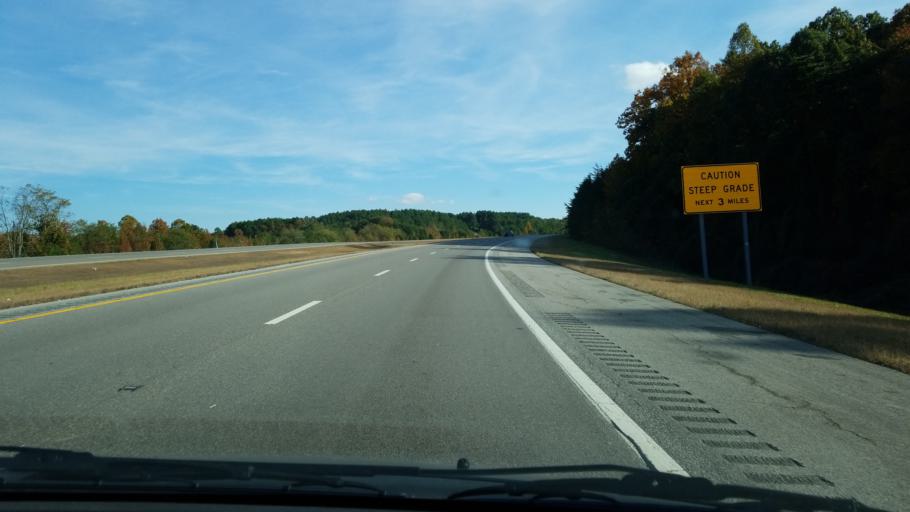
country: US
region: Tennessee
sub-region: Hamilton County
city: Sale Creek
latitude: 35.3436
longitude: -85.1711
